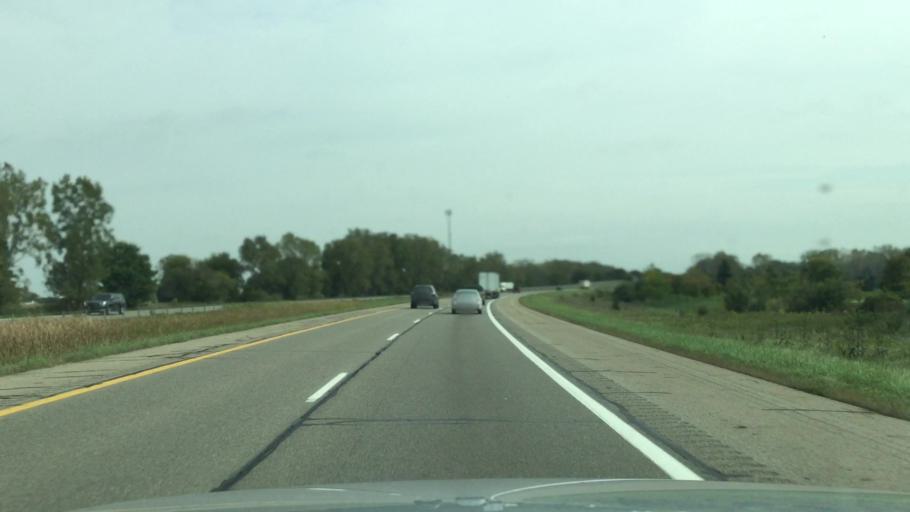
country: US
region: Michigan
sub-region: Shiawassee County
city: Durand
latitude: 42.9609
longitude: -83.9611
